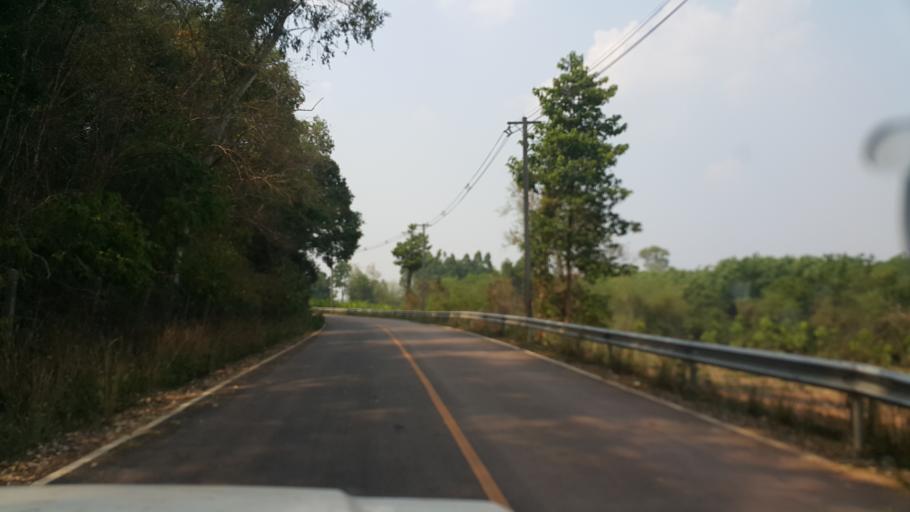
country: TH
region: Nakhon Phanom
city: Ban Phaeng
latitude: 17.9530
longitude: 104.1617
